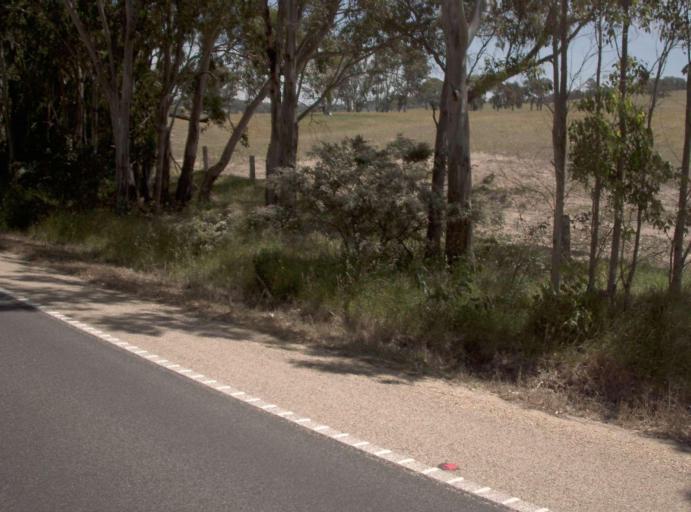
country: AU
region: Victoria
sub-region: East Gippsland
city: Bairnsdale
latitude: -37.7562
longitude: 147.7114
